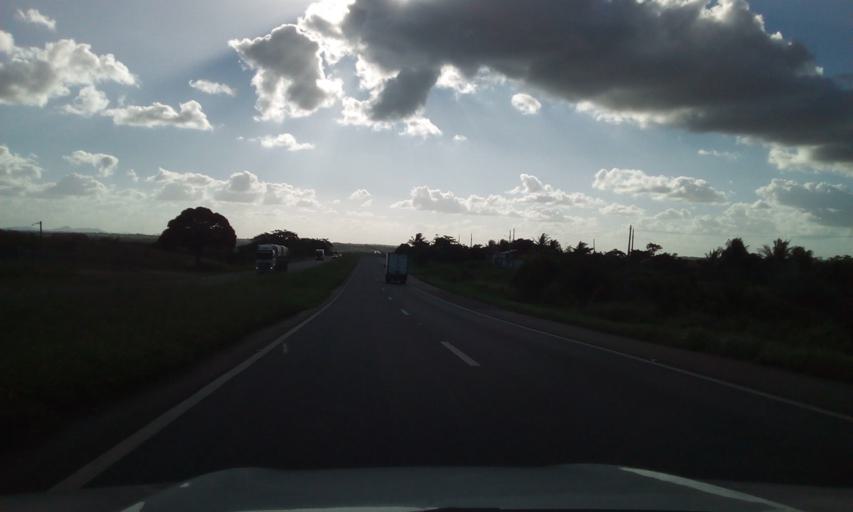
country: BR
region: Paraiba
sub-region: Cruz Do Espirito Santo
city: Cruz do Espirito Santo
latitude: -7.2000
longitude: -35.1622
